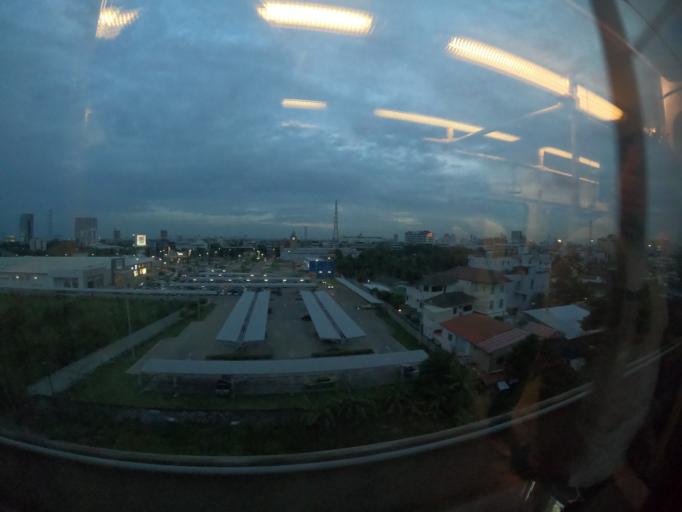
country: TH
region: Bangkok
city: Suan Luang
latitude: 13.7392
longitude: 100.6352
